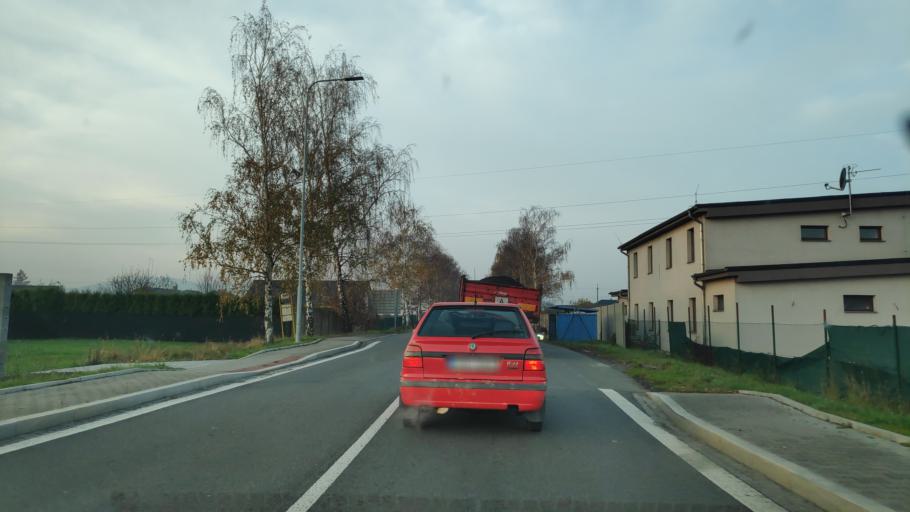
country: CZ
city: Sviadnov
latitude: 49.6947
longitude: 18.3202
